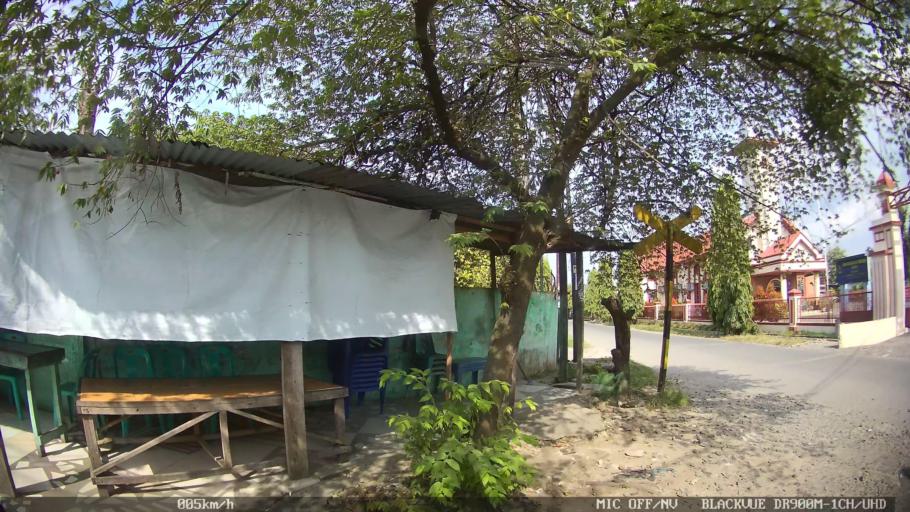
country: ID
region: North Sumatra
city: Binjai
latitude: 3.6106
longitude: 98.4962
